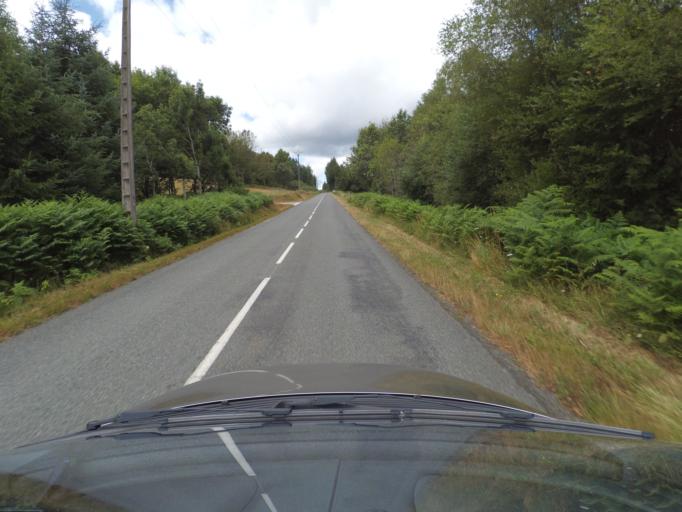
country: FR
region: Limousin
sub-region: Departement de la Haute-Vienne
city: Peyrat-le-Chateau
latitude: 45.8814
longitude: 1.8948
